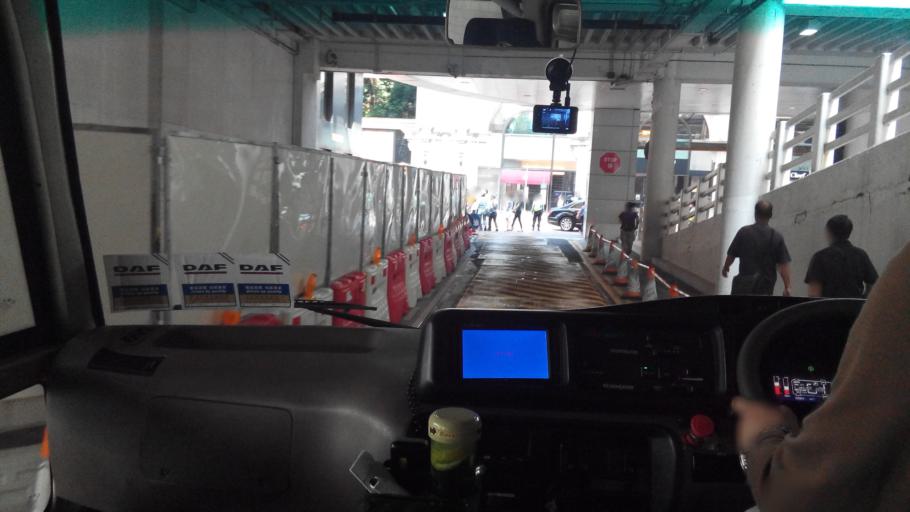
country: HK
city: Hong Kong
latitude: 22.2993
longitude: 114.1675
